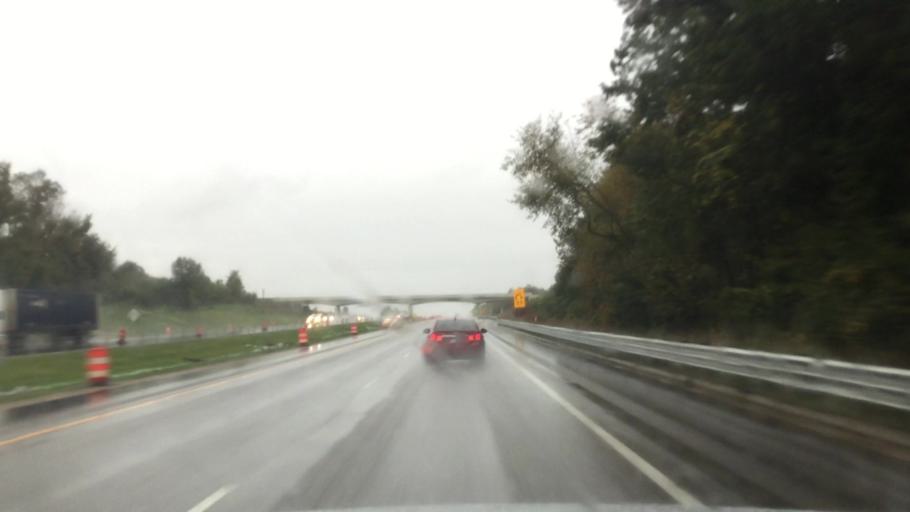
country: US
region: Michigan
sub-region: Van Buren County
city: Decatur
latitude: 42.1967
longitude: -86.0473
